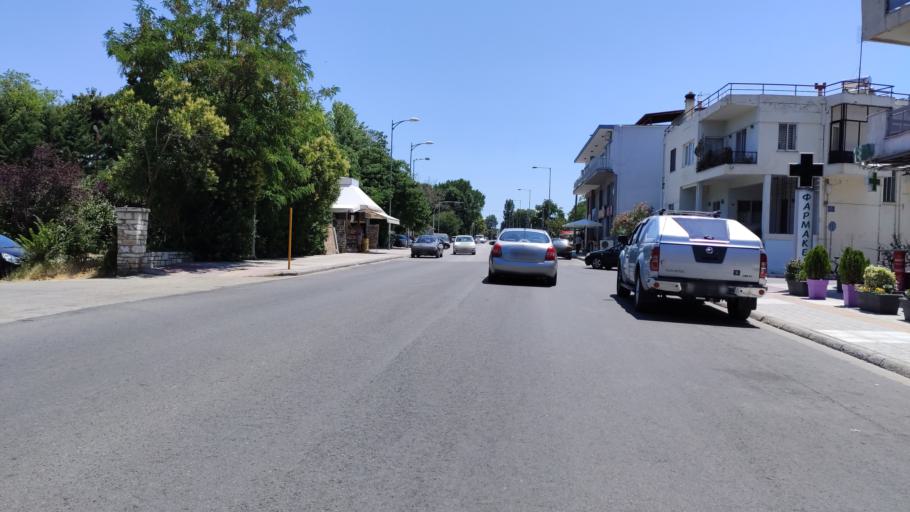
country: GR
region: East Macedonia and Thrace
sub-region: Nomos Rodopis
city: Komotini
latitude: 41.1128
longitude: 25.4111
